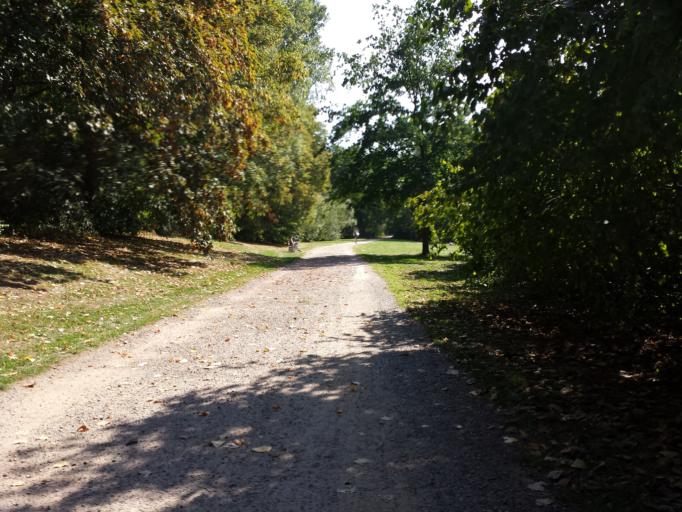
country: DE
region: Bremen
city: Bremen
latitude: 53.0650
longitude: 8.8103
